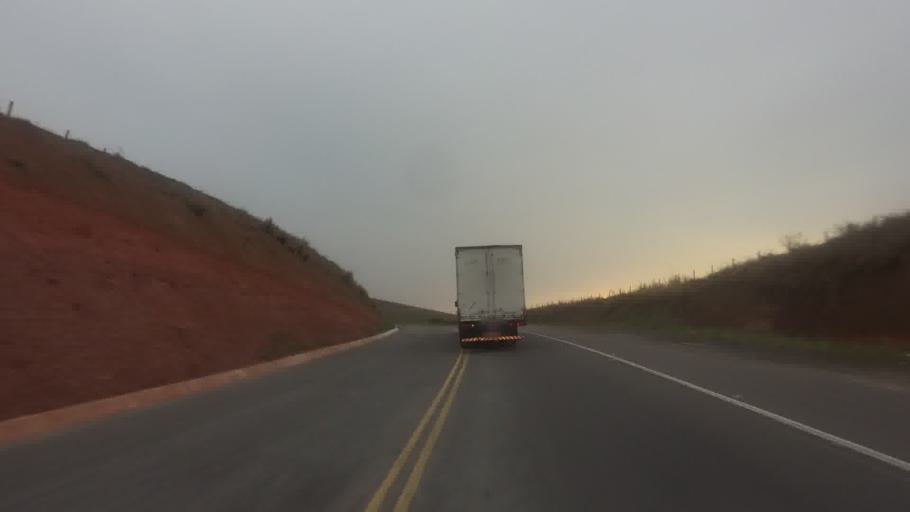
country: BR
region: Minas Gerais
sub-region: Recreio
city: Recreio
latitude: -21.6882
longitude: -42.4076
